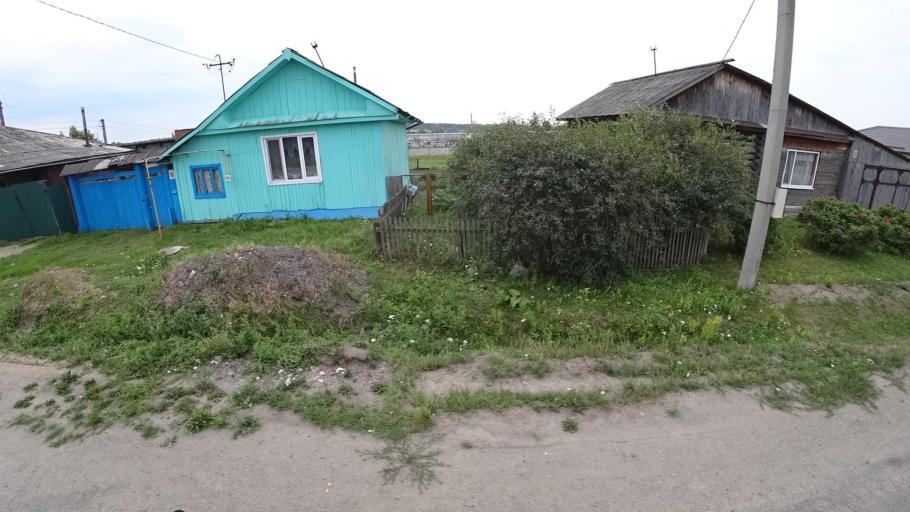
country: RU
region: Sverdlovsk
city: Kamyshlov
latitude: 56.8466
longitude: 62.7391
